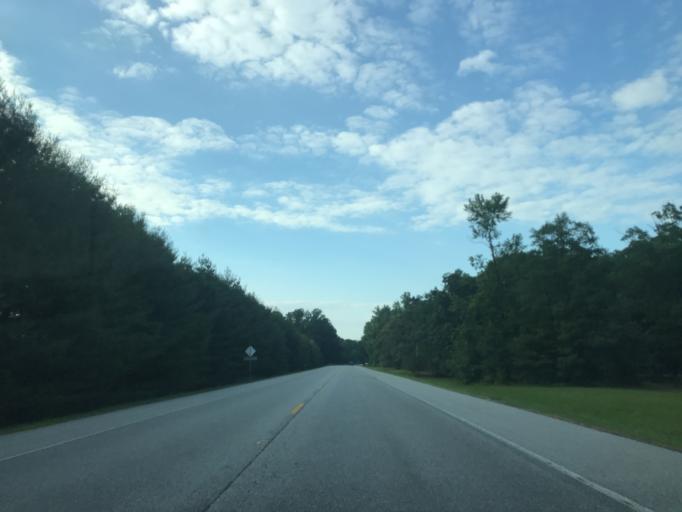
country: US
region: Maryland
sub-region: Caroline County
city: Federalsburg
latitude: 38.7569
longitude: -75.7900
